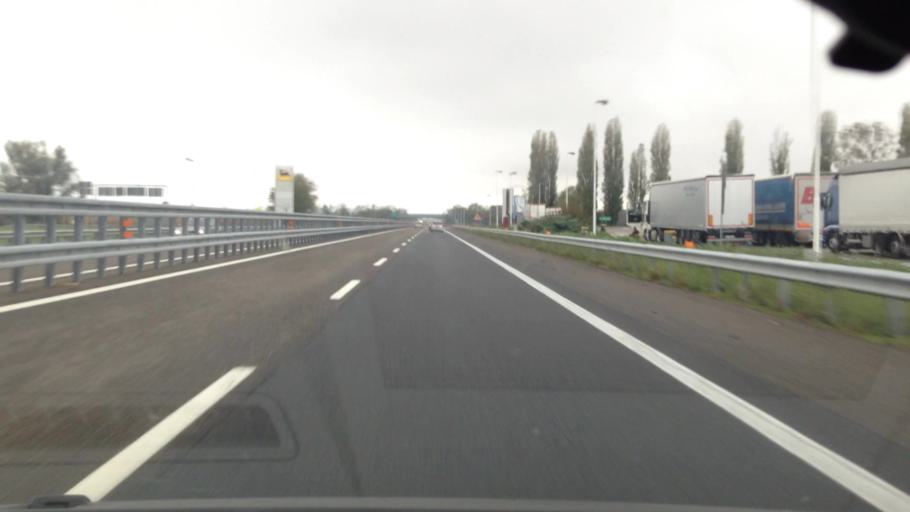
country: IT
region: Piedmont
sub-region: Provincia di Asti
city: Villanova d'Asti
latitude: 44.9499
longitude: 7.9521
